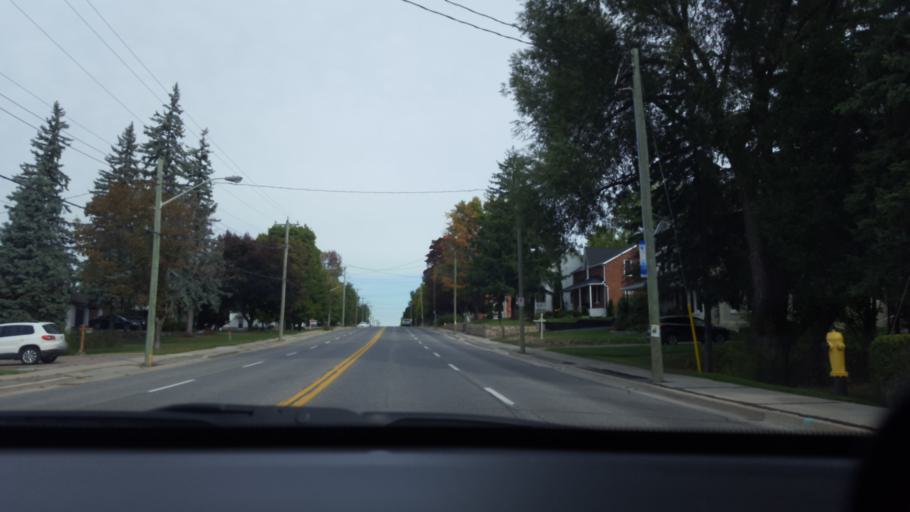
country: CA
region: Ontario
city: Vaughan
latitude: 43.9240
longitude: -79.5270
